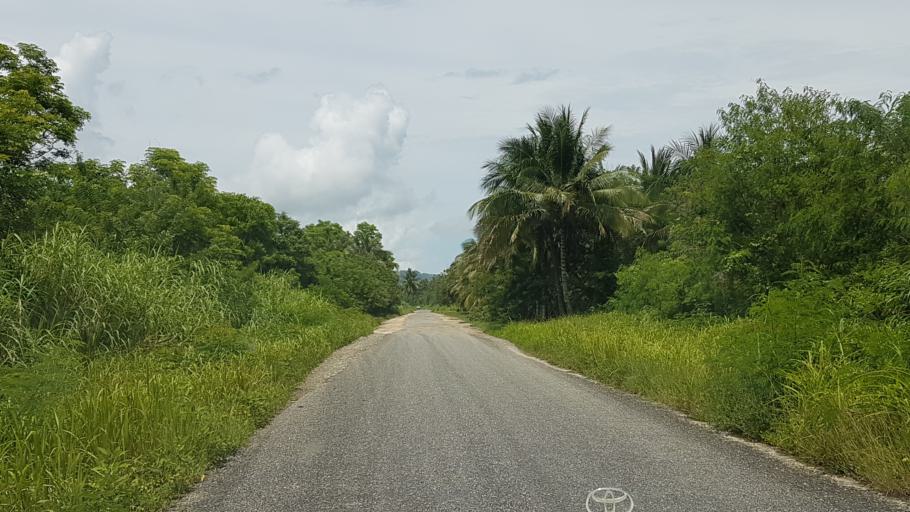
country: PG
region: Madang
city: Madang
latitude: -4.5447
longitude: 145.4964
